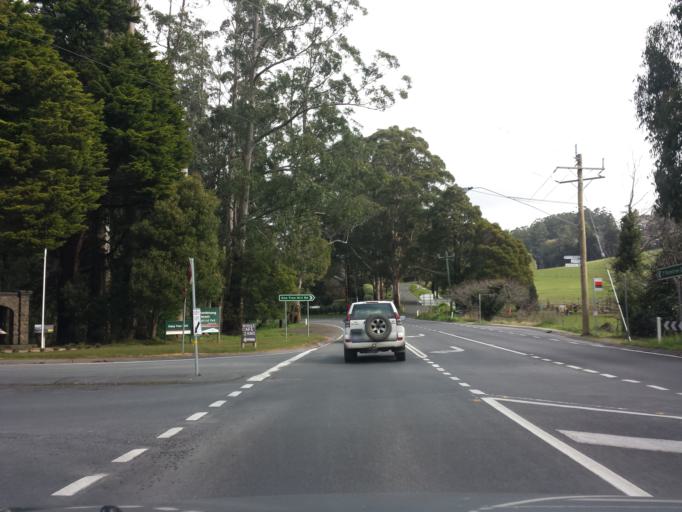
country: AU
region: Victoria
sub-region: Yarra Ranges
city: Ferny Creek
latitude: -37.8752
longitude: 145.3429
